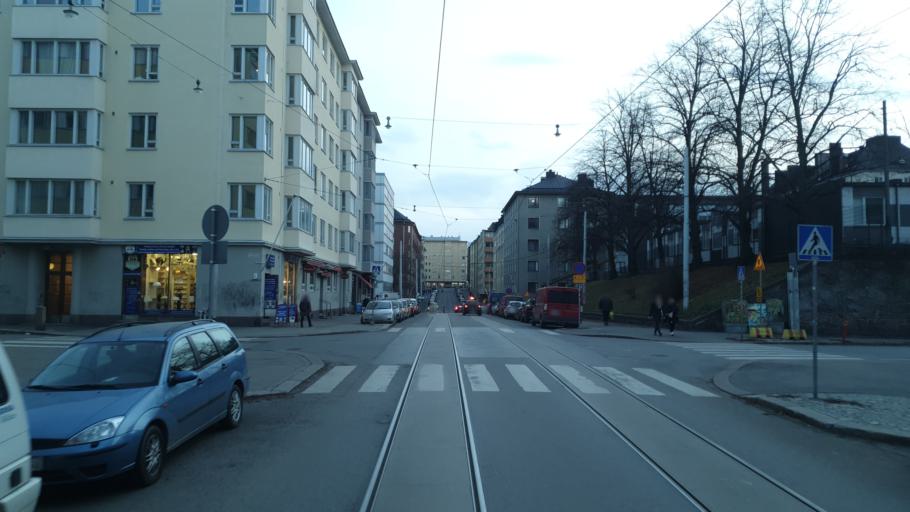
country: FI
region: Uusimaa
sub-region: Helsinki
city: Helsinki
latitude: 60.1885
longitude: 24.9530
